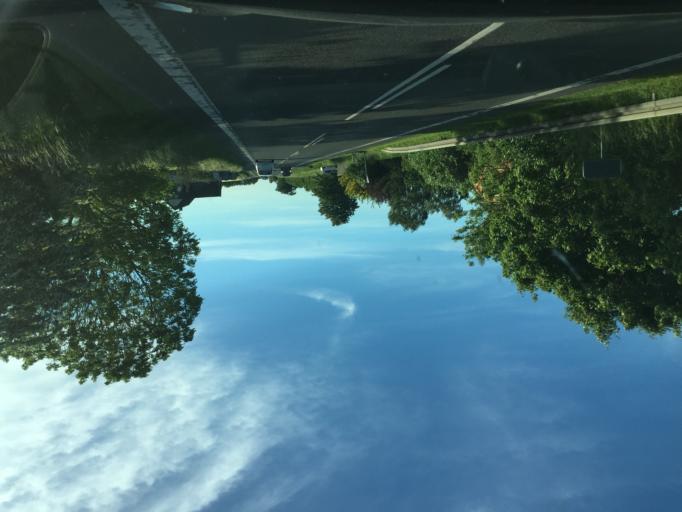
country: DK
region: Zealand
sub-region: Slagelse Kommune
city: Forlev
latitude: 55.3759
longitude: 11.2942
